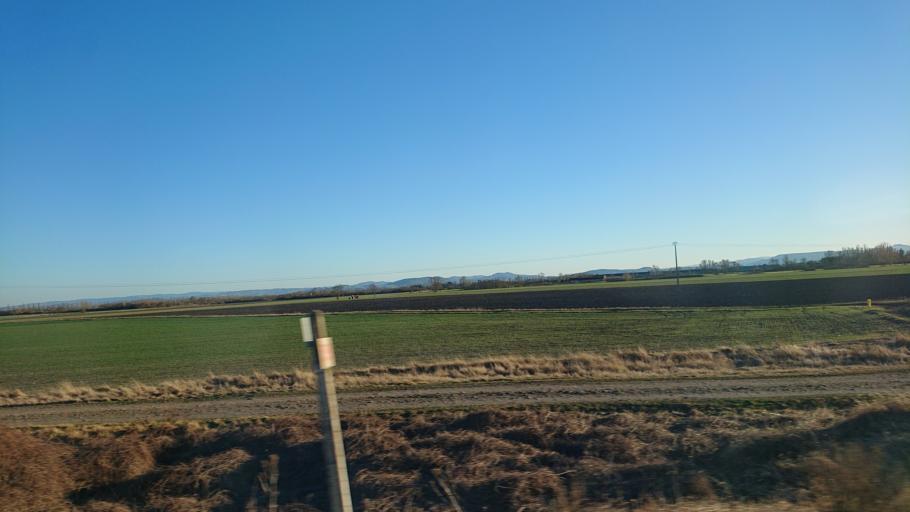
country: FR
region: Auvergne
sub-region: Departement du Puy-de-Dome
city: Ennezat
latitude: 45.9081
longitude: 3.1962
